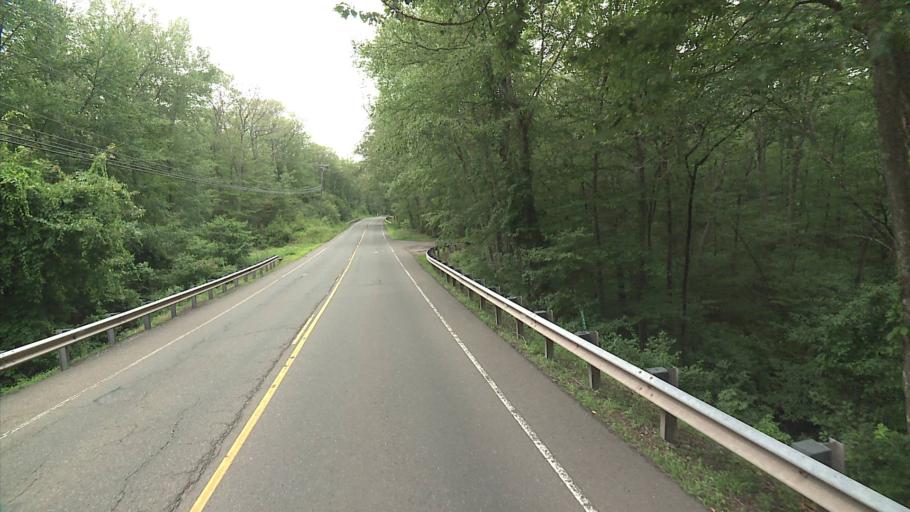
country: US
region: Connecticut
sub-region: Middlesex County
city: Clinton
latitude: 41.3568
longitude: -72.5364
